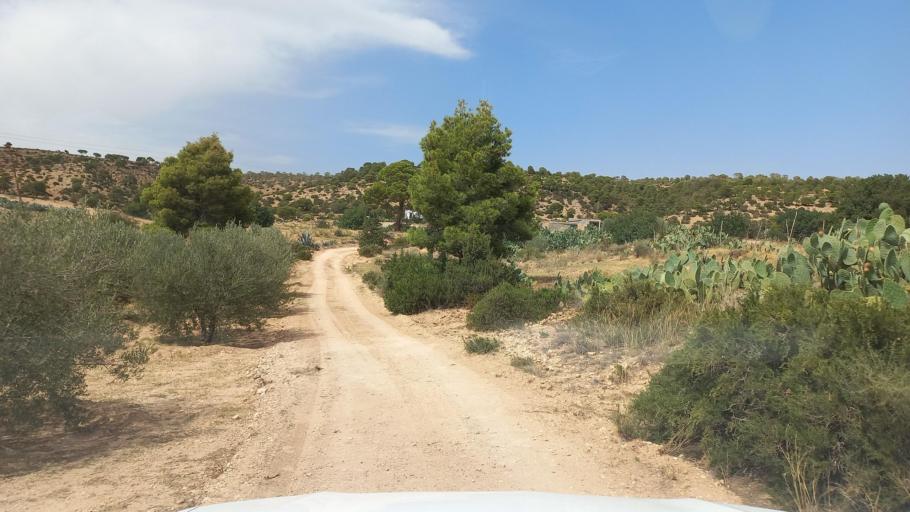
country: TN
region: Al Qasrayn
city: Kasserine
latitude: 35.3720
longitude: 8.8916
